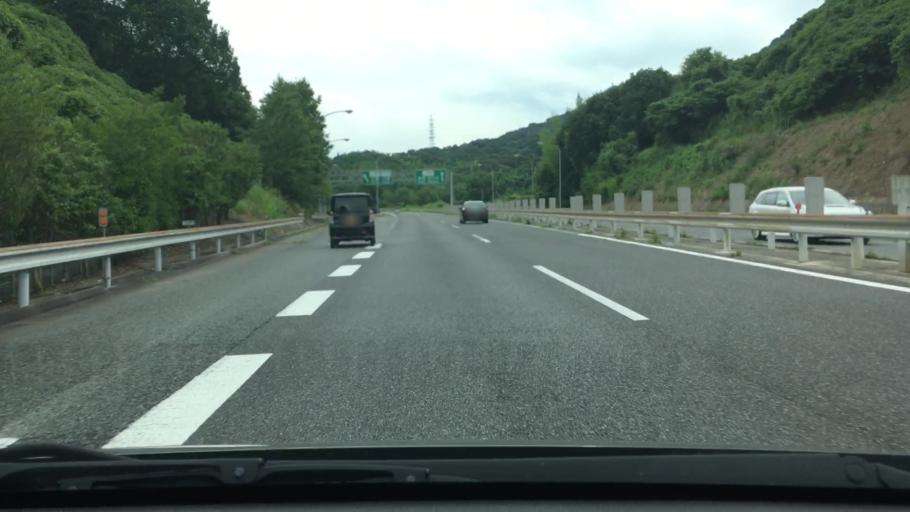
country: JP
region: Hiroshima
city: Hatsukaichi
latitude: 34.3388
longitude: 132.2985
